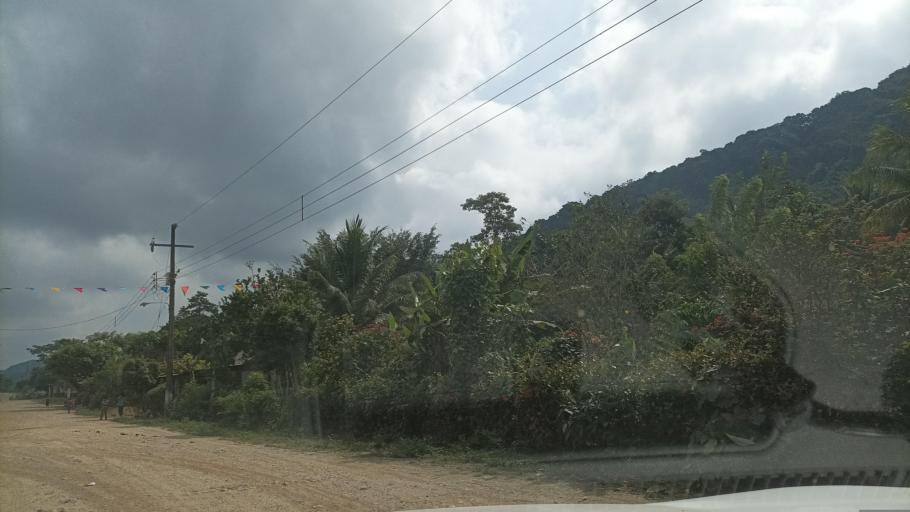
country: MX
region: Veracruz
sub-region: Uxpanapa
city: Poblado Cinco
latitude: 17.4618
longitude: -94.6046
